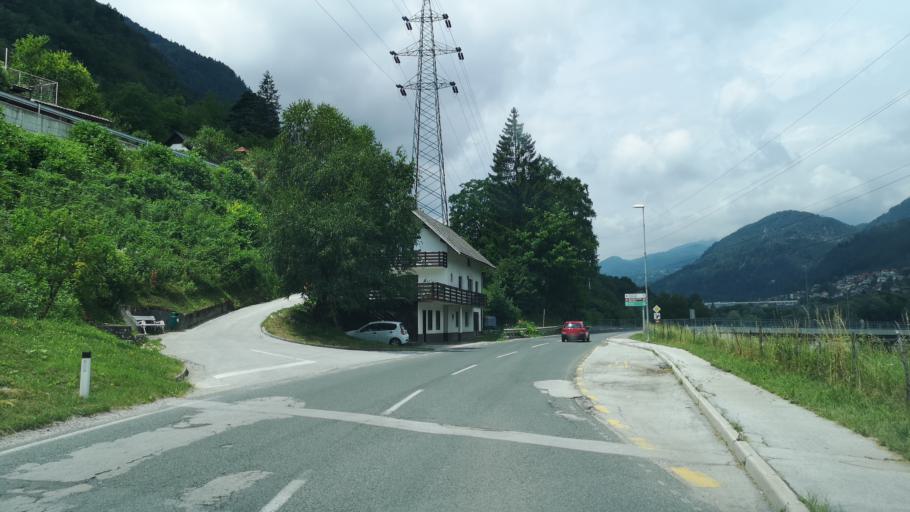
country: SI
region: Jesenice
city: Slovenski Javornik
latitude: 46.4220
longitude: 14.0837
